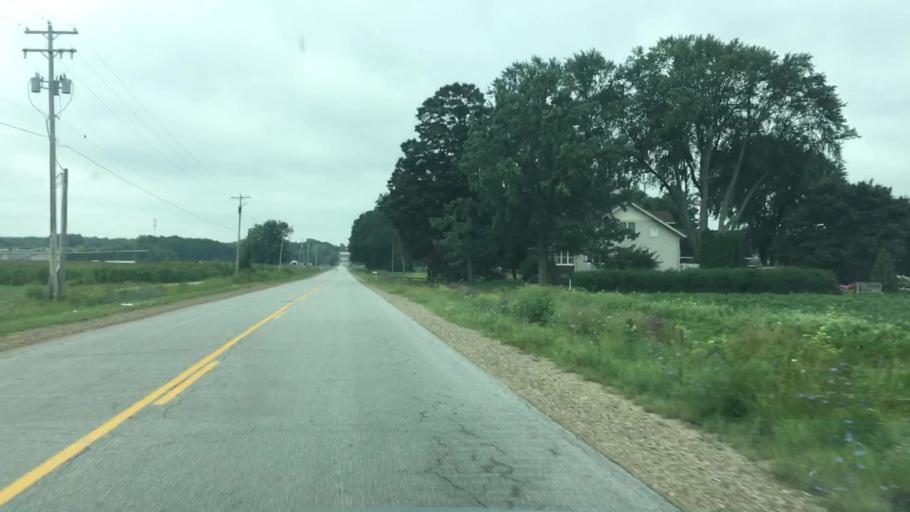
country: US
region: Michigan
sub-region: Ottawa County
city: Hudsonville
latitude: 42.8679
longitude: -85.8365
